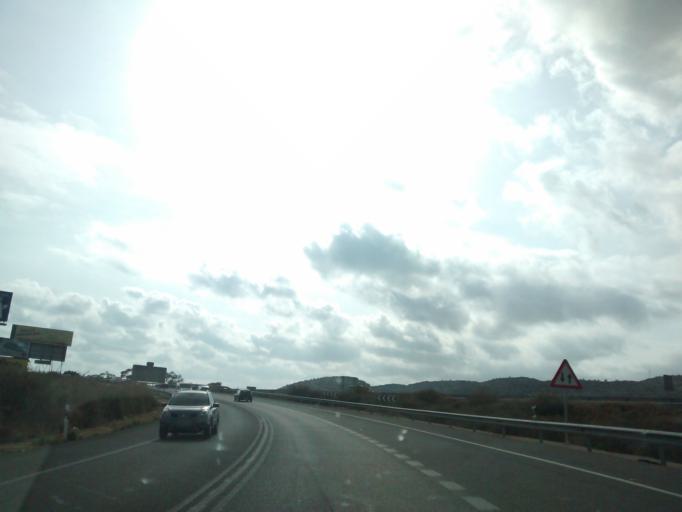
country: ES
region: Valencia
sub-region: Provincia de Alicante
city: el Campello
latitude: 38.4485
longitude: -0.3810
